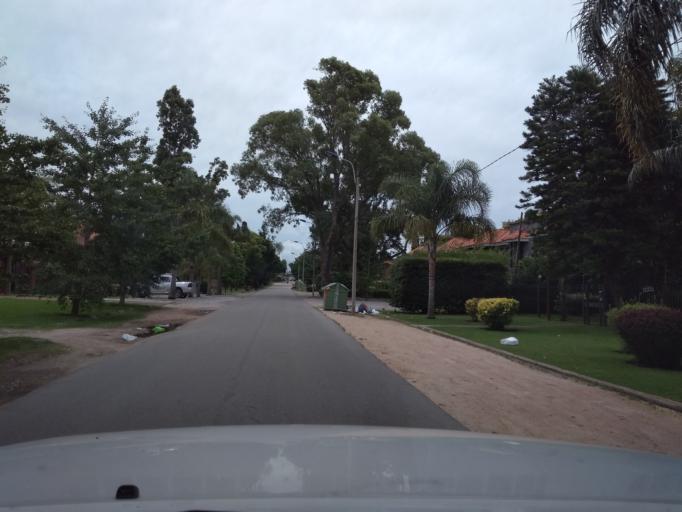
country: UY
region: Canelones
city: Paso de Carrasco
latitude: -34.8806
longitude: -56.0564
